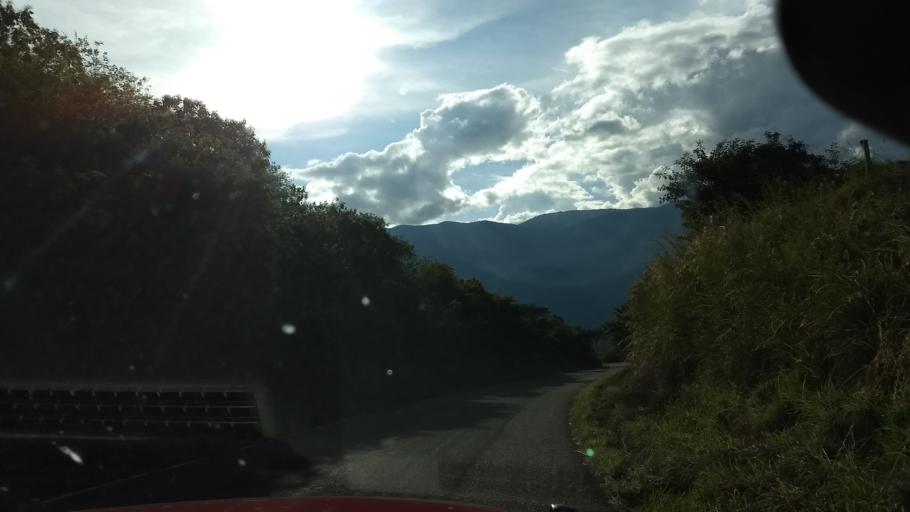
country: MX
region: Colima
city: Suchitlan
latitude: 19.4586
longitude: -103.7956
